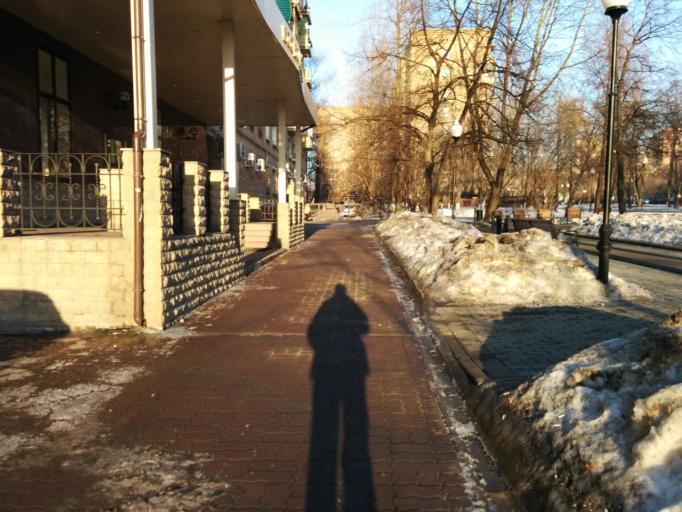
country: RU
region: Moscow
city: Novyye Cheremushki
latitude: 55.7264
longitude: 37.5855
